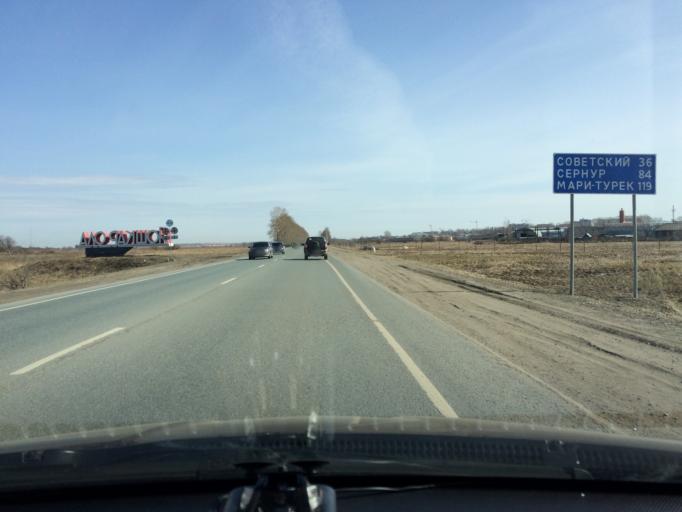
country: RU
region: Mariy-El
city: Yoshkar-Ola
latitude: 56.6473
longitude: 47.9392
